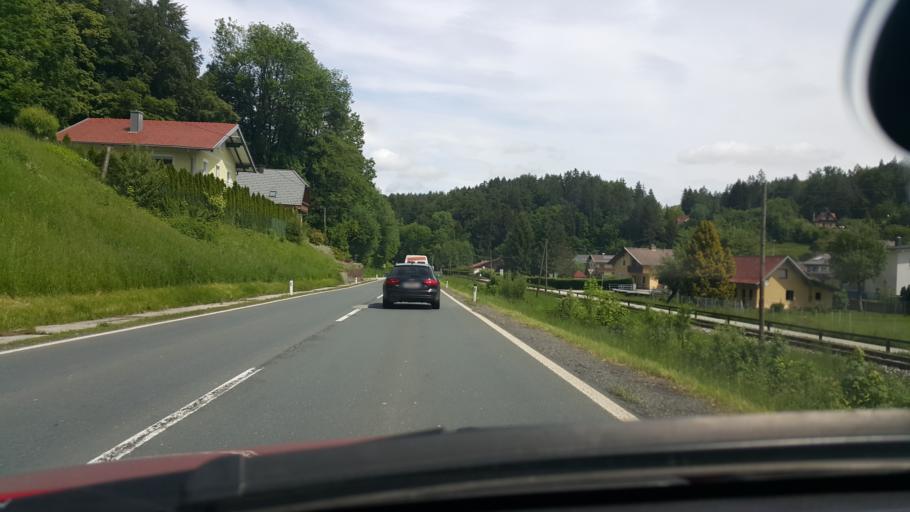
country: AT
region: Carinthia
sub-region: Politischer Bezirk Klagenfurt Land
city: Maria Rain
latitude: 46.5720
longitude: 14.2858
